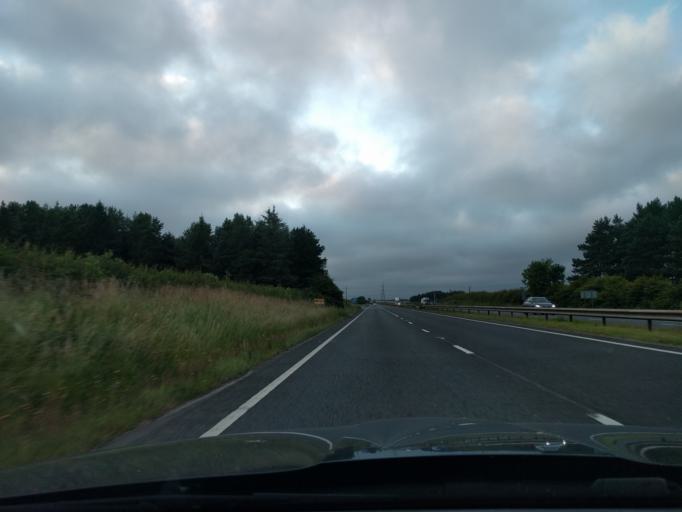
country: GB
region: England
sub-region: Northumberland
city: Stannington
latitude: 55.1201
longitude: -1.6711
